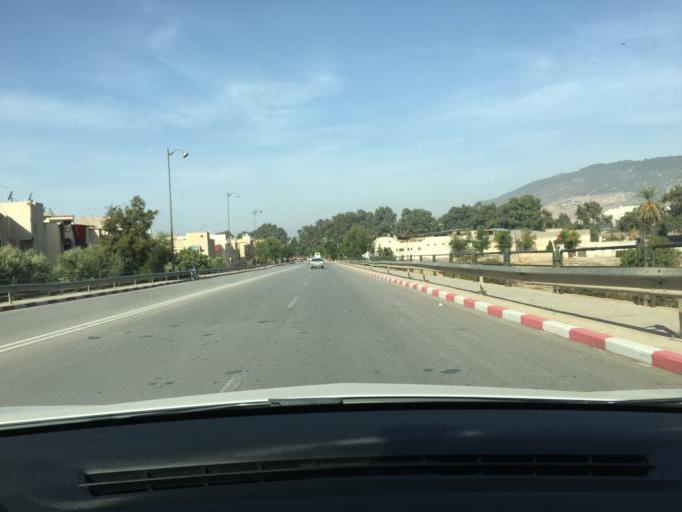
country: MA
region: Fes-Boulemane
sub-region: Fes
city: Fes
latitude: 34.0392
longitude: -5.0252
